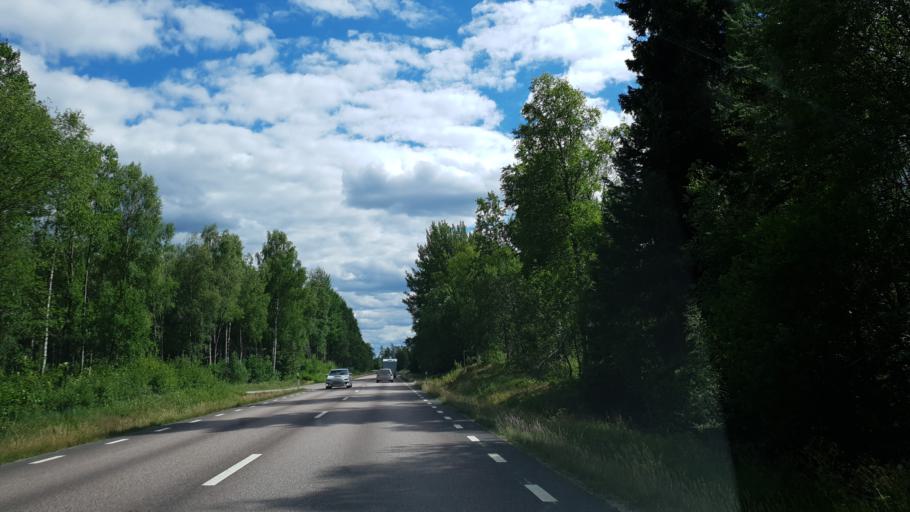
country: SE
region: Kronoberg
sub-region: Lessebo Kommun
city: Lessebo
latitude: 56.8403
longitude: 15.3910
